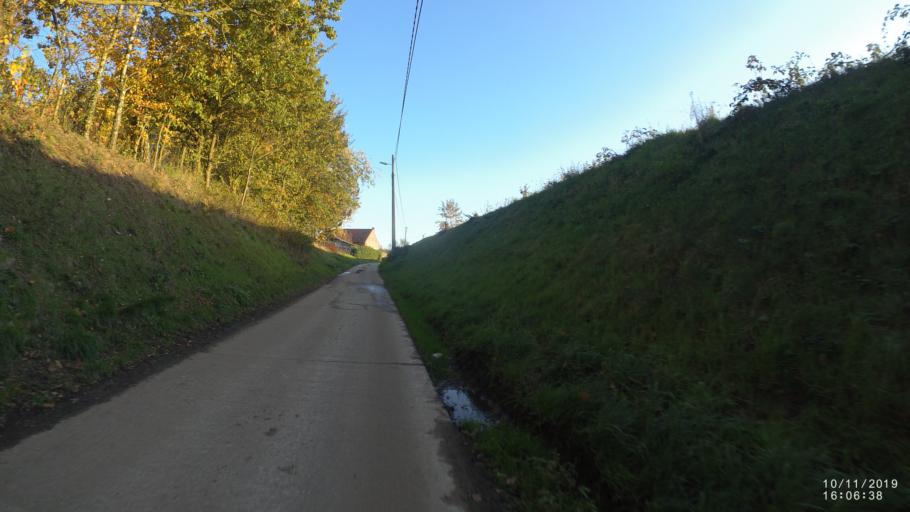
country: BE
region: Flanders
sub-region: Provincie Vlaams-Brabant
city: Lubbeek
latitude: 50.8995
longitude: 4.8546
